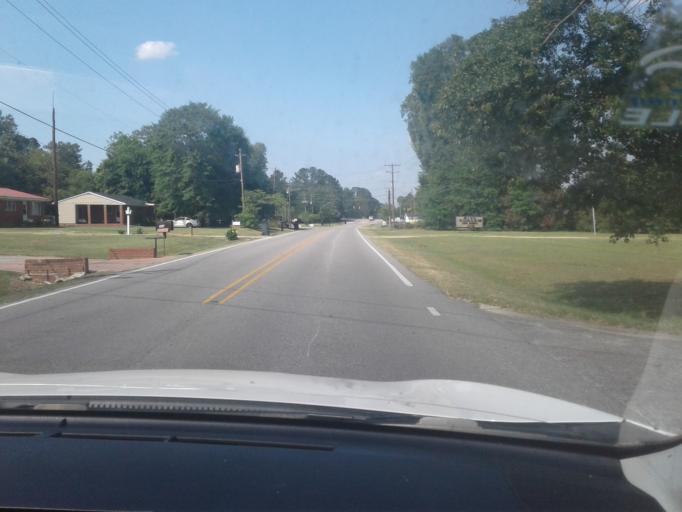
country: US
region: North Carolina
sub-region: Harnett County
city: Erwin
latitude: 35.3261
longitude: -78.6625
